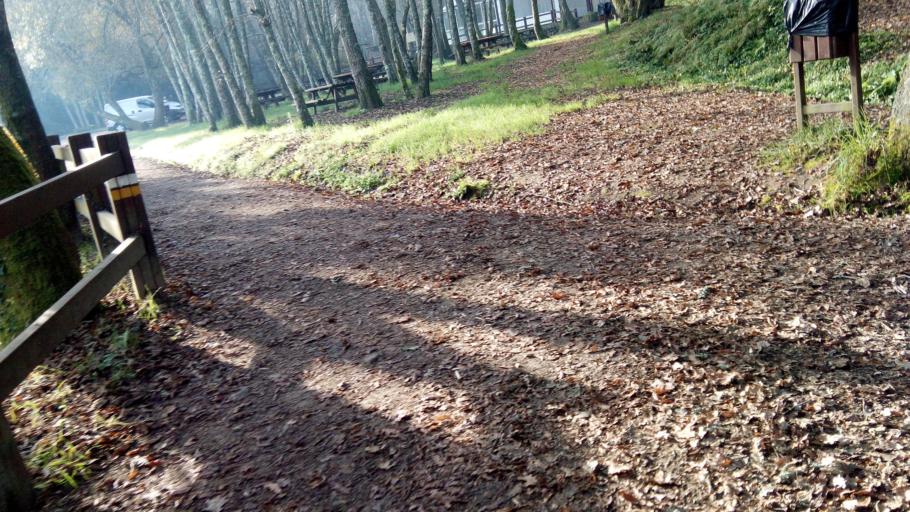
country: ES
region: Galicia
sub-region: Provincia de Pontevedra
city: Meis
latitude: 42.4909
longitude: -8.7520
